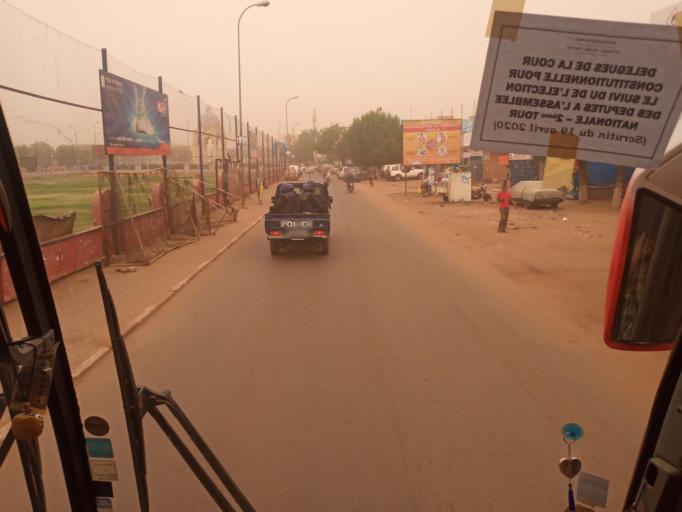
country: ML
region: Bamako
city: Bamako
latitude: 12.6514
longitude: -7.9914
